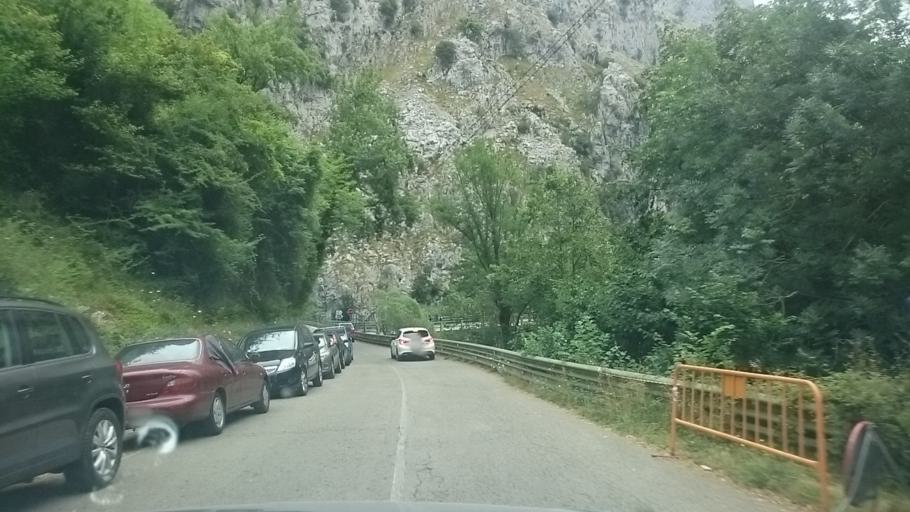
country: ES
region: Asturias
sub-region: Province of Asturias
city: Carrena
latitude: 43.2577
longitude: -4.8315
